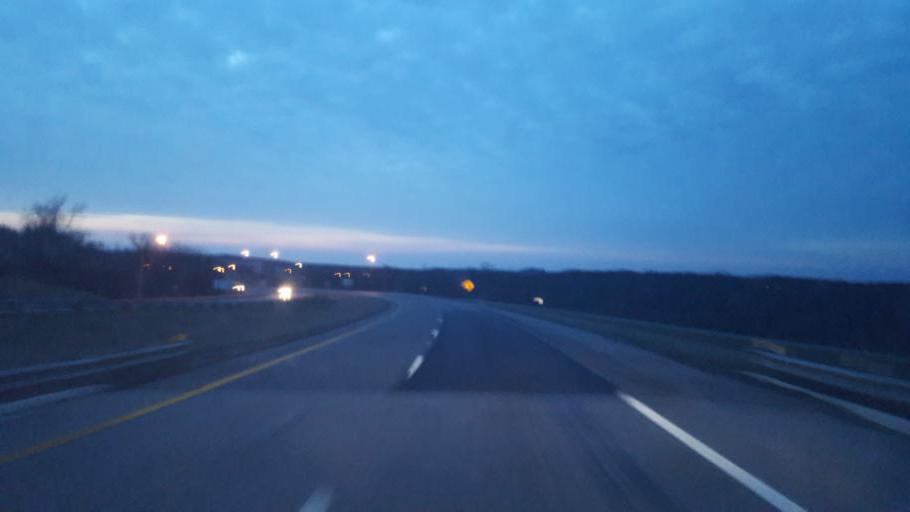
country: US
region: Ohio
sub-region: Jackson County
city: Jackson
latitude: 39.0528
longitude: -82.6185
